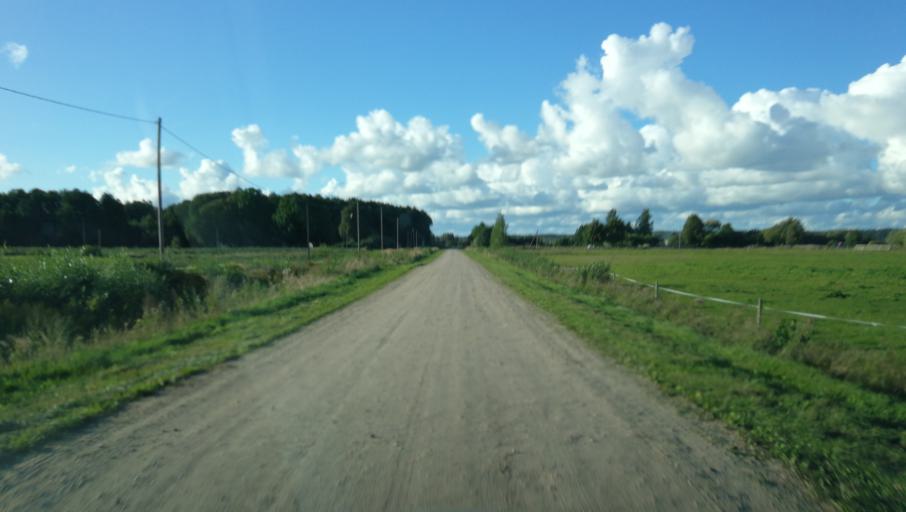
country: LV
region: Riga
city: Jaunciems
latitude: 57.0729
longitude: 24.2331
